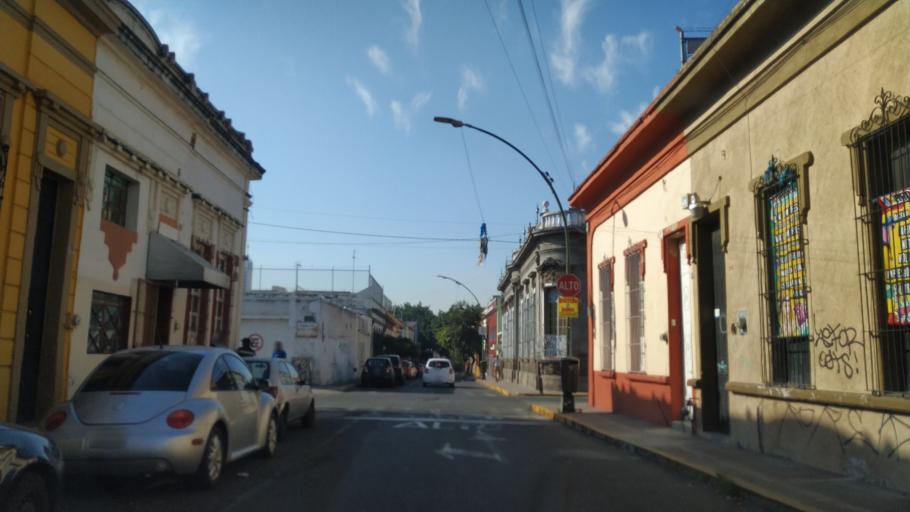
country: MX
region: Jalisco
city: Guadalajara
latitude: 20.6711
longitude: -103.3508
